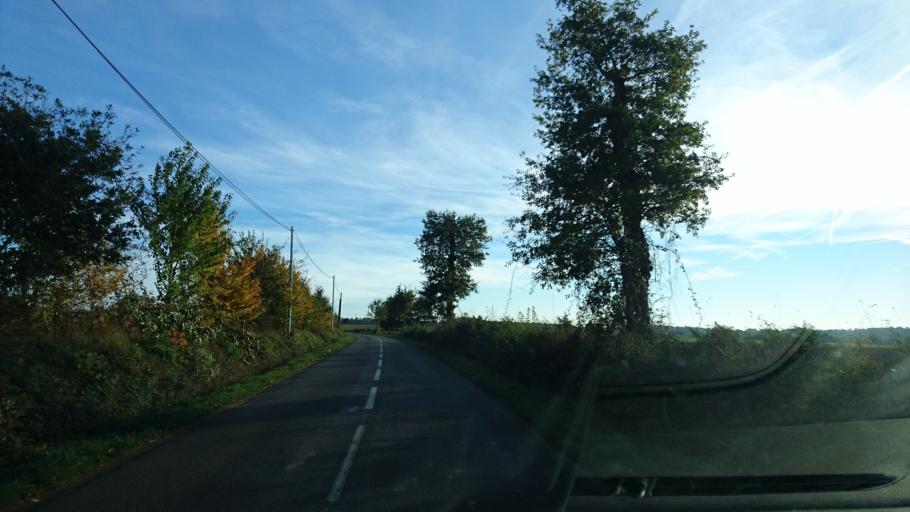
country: FR
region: Brittany
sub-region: Departement d'Ille-et-Vilaine
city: Bruz
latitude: 48.0104
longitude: -1.7478
